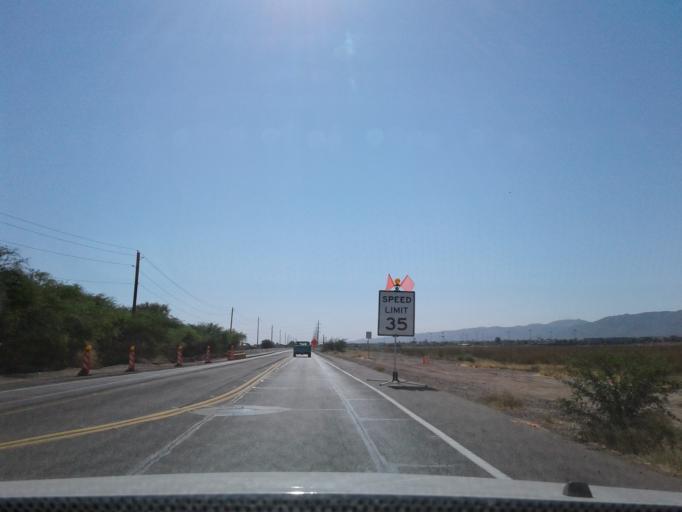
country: US
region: Arizona
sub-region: Maricopa County
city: Laveen
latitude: 33.3773
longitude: -112.1938
